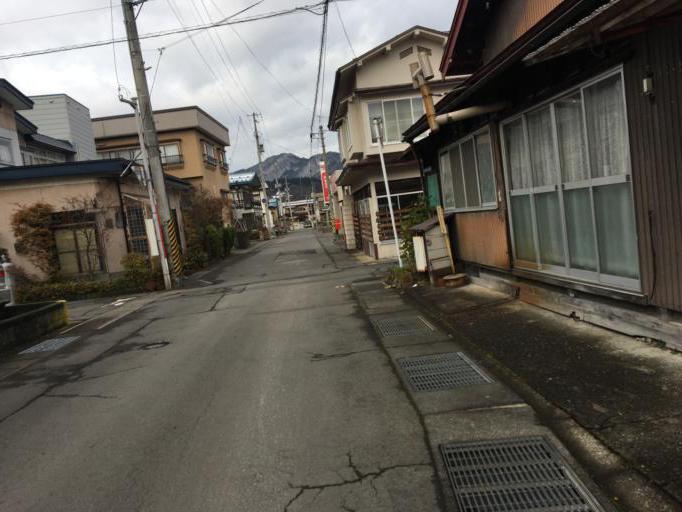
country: JP
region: Aomori
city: Hirosaki
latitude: 40.5208
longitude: 140.5697
